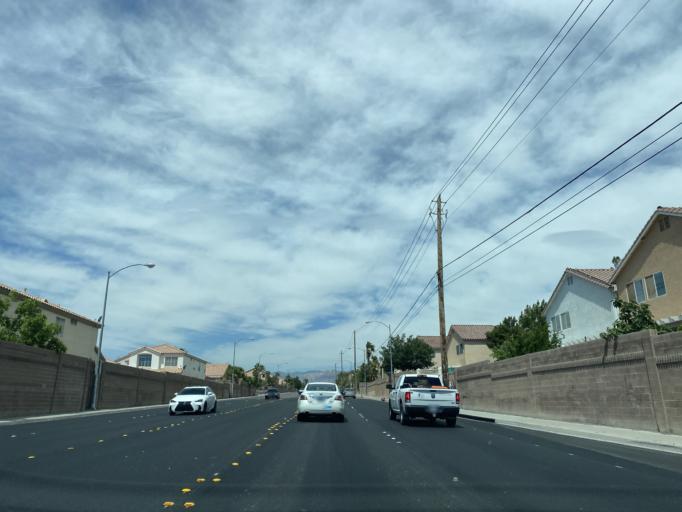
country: US
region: Nevada
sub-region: Clark County
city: Spring Valley
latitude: 36.1256
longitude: -115.2617
